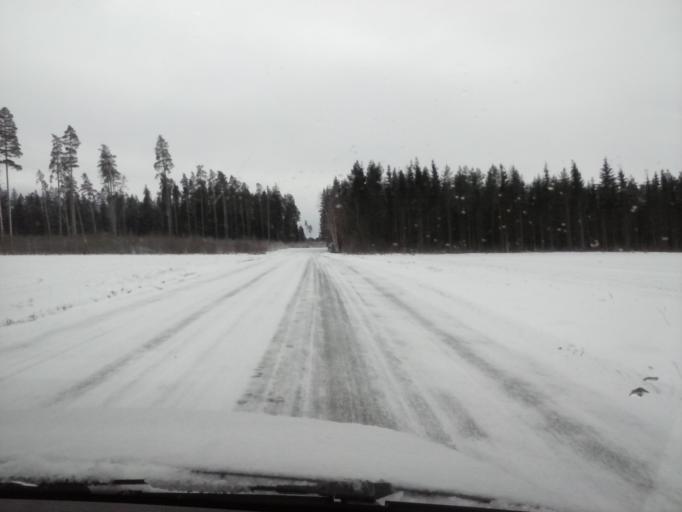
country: EE
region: Polvamaa
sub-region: Polva linn
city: Polva
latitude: 58.1713
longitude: 27.0819
